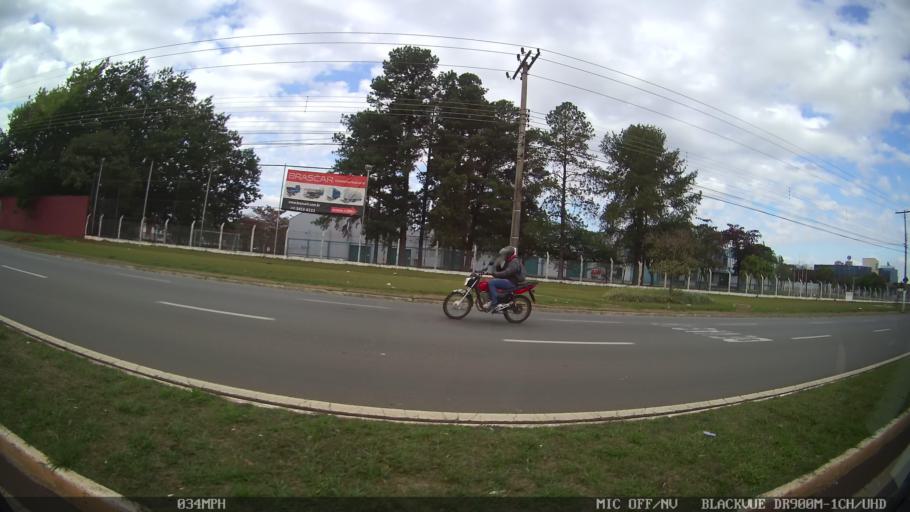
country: BR
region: Sao Paulo
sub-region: Limeira
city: Limeira
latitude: -22.5499
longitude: -47.3790
